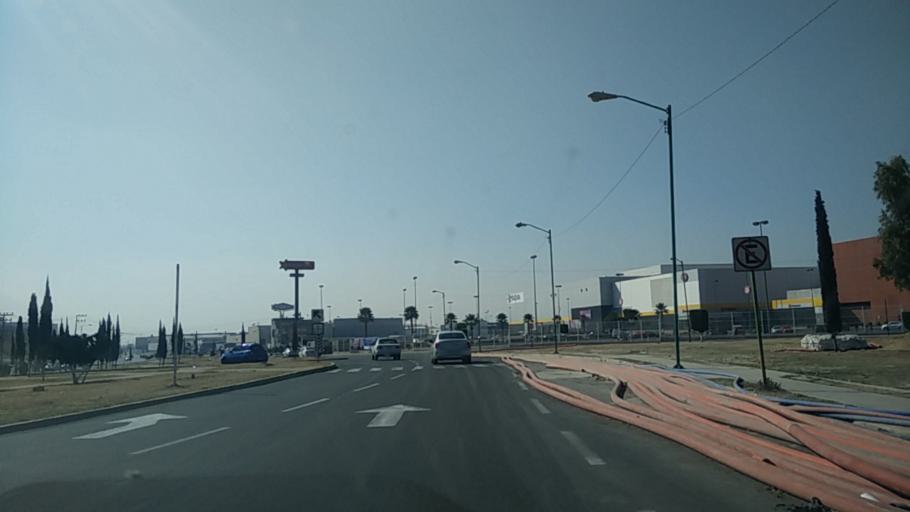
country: MX
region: Mexico
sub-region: Atenco
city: Colonia el Salado
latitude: 19.5863
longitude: -99.0223
